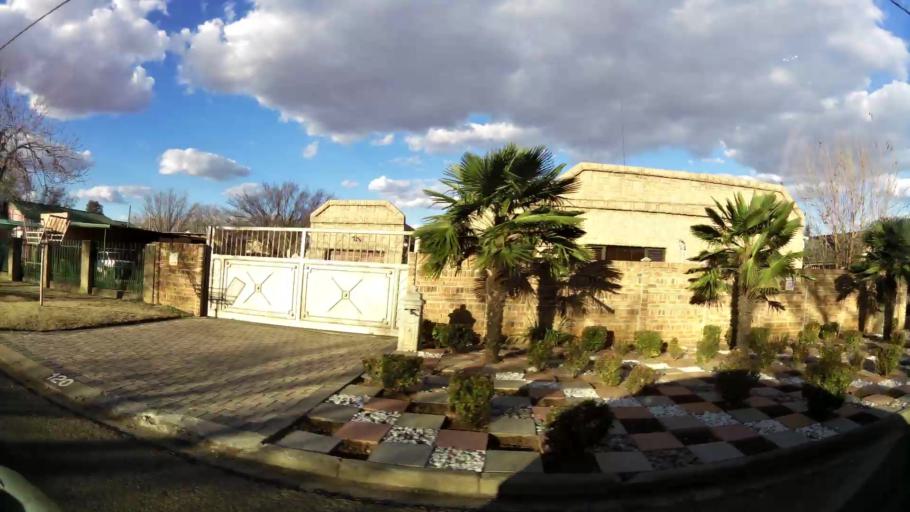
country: ZA
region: North-West
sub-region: Dr Kenneth Kaunda District Municipality
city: Potchefstroom
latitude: -26.7338
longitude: 27.0839
